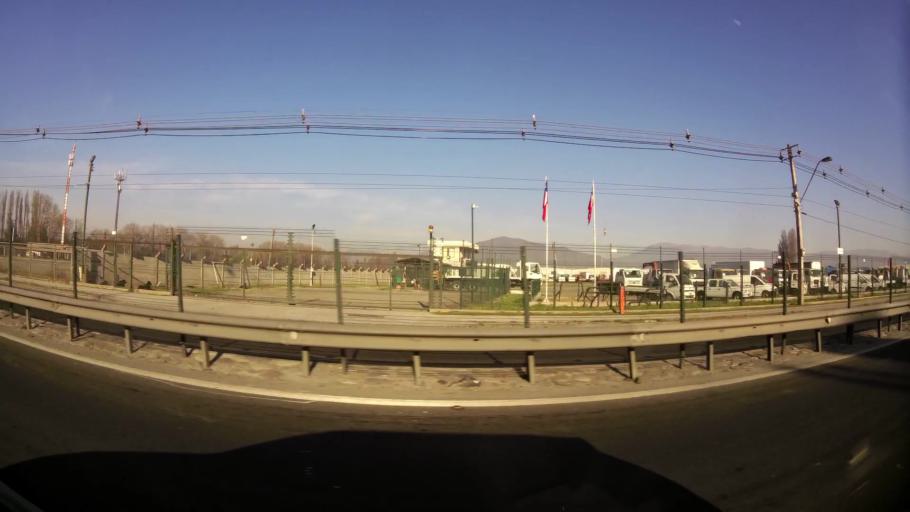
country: CL
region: Santiago Metropolitan
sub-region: Provincia de Santiago
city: Lo Prado
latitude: -33.4618
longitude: -70.7641
